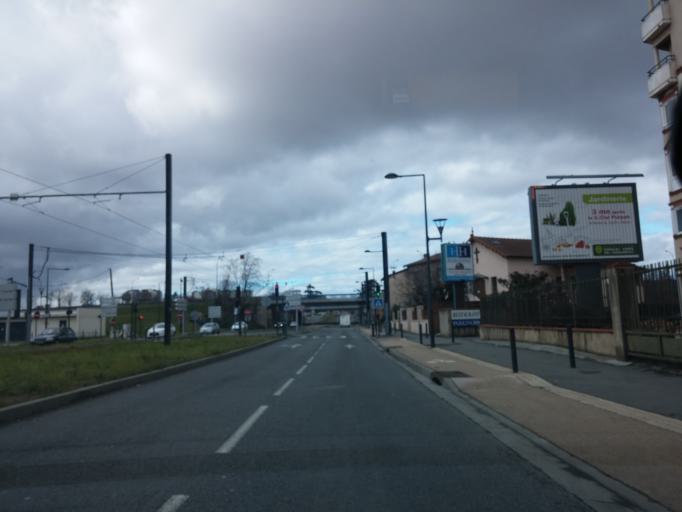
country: FR
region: Midi-Pyrenees
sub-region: Departement de la Haute-Garonne
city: Blagnac
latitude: 43.6043
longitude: 1.4058
